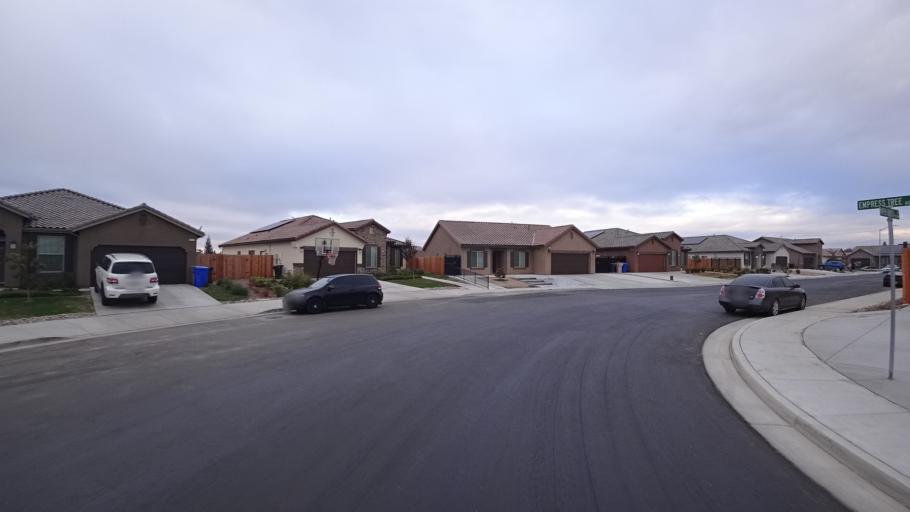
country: US
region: California
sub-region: Kern County
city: Greenfield
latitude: 35.2935
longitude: -119.0694
